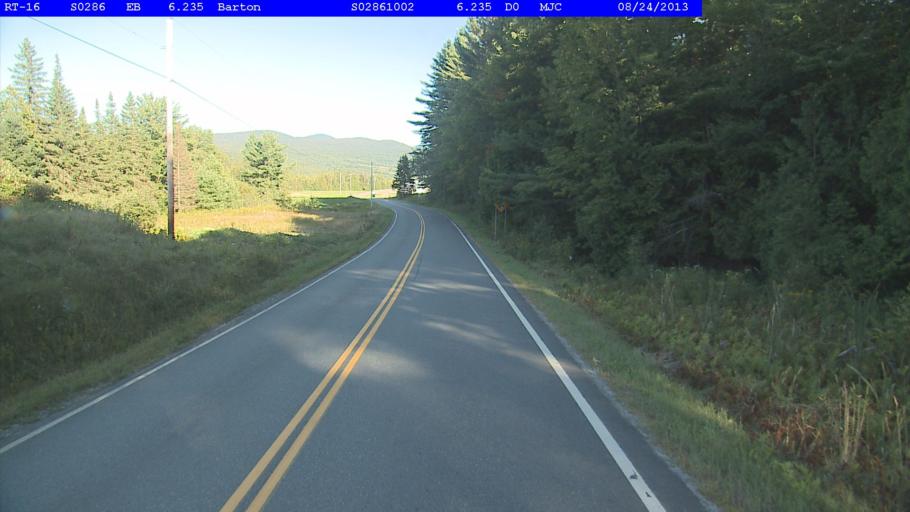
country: US
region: Vermont
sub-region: Orleans County
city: Newport
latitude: 44.7818
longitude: -72.0841
